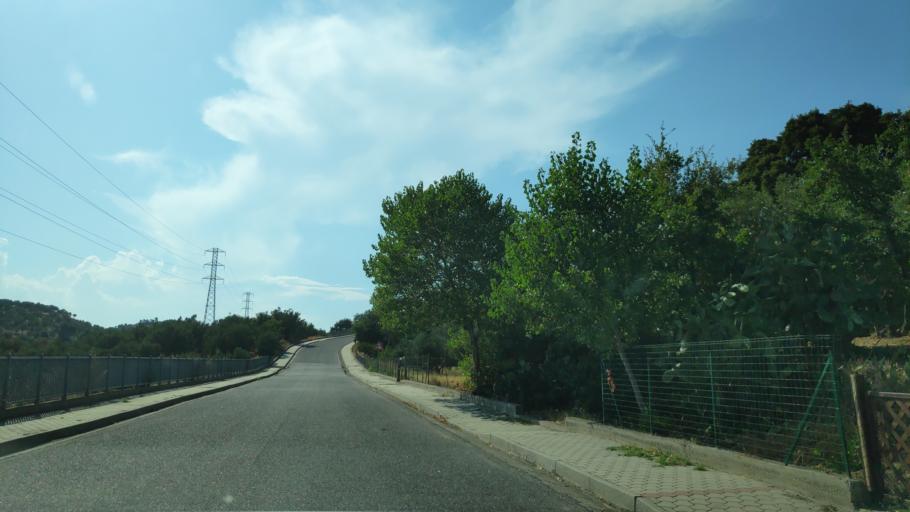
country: IT
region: Calabria
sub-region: Provincia di Catanzaro
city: Soverato Superiore
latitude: 38.6855
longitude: 16.5391
